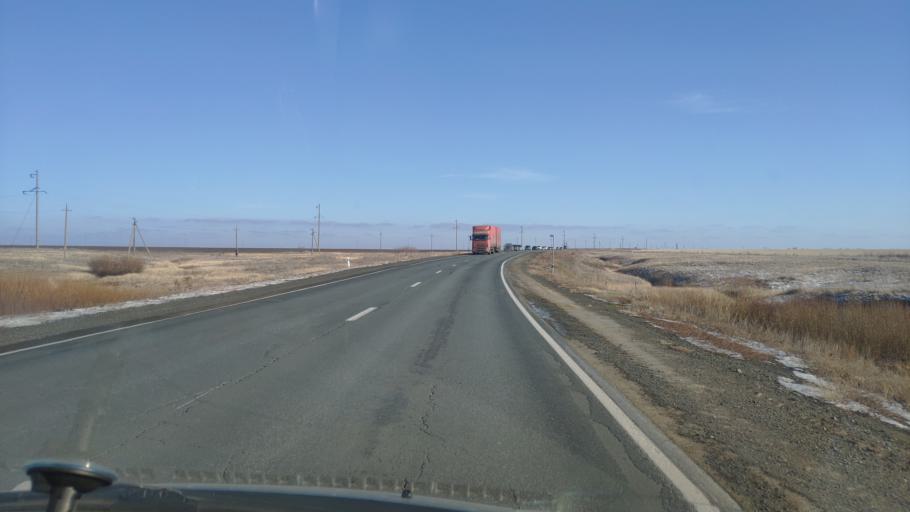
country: RU
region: Orenburg
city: Mednogorsk
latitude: 51.4354
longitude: 57.8920
